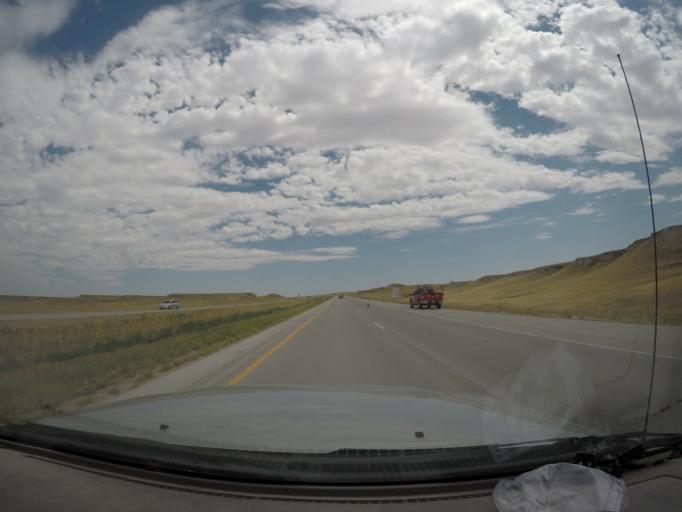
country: US
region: Nebraska
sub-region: Cheyenne County
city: Sidney
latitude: 41.1193
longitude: -103.0159
